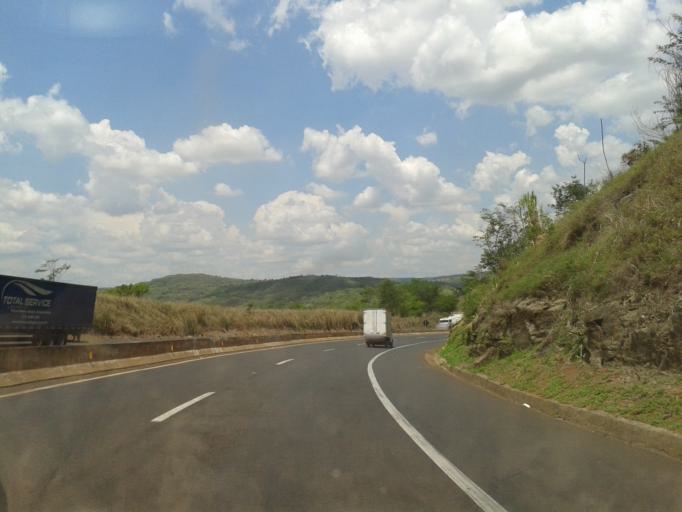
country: BR
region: Minas Gerais
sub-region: Araguari
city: Araguari
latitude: -18.7621
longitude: -48.2411
